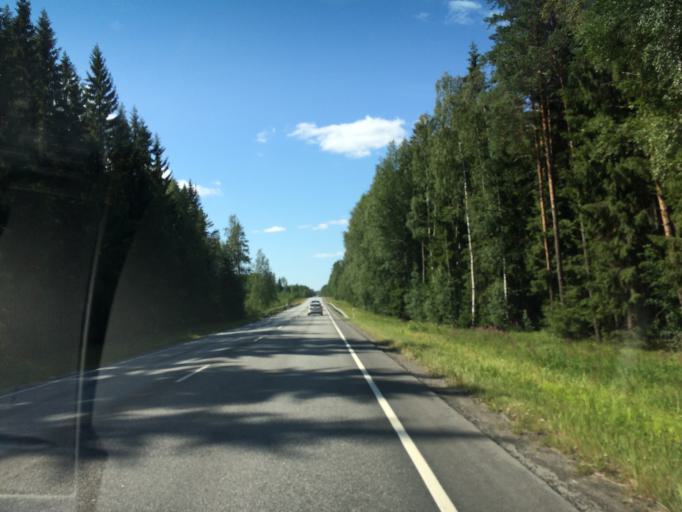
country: FI
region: Pirkanmaa
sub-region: Lounais-Pirkanmaa
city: Kiikoinen
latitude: 61.4757
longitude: 22.4510
